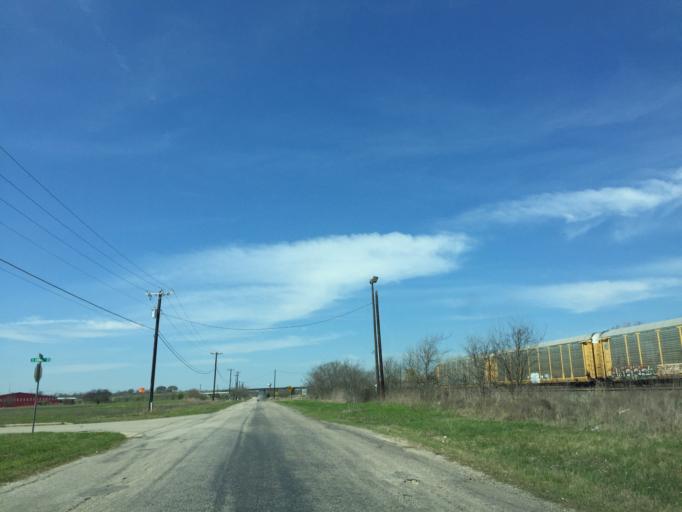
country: US
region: Texas
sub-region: Williamson County
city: Taylor
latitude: 30.5661
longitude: -97.4262
